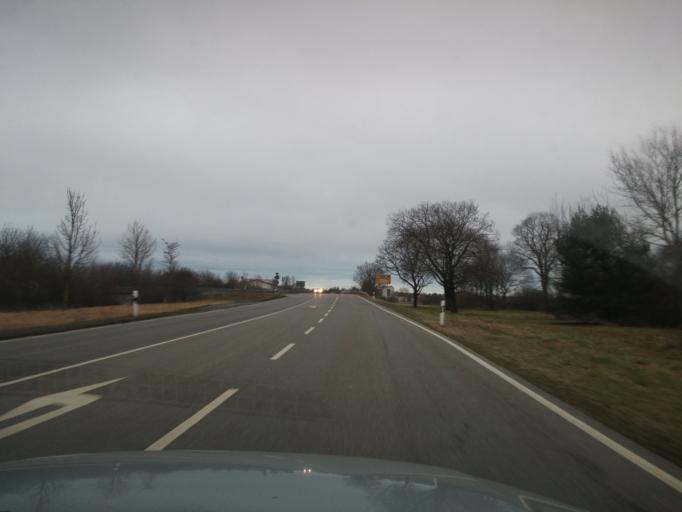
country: DE
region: Bavaria
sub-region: Upper Bavaria
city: Aschheim
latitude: 48.1599
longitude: 11.7217
